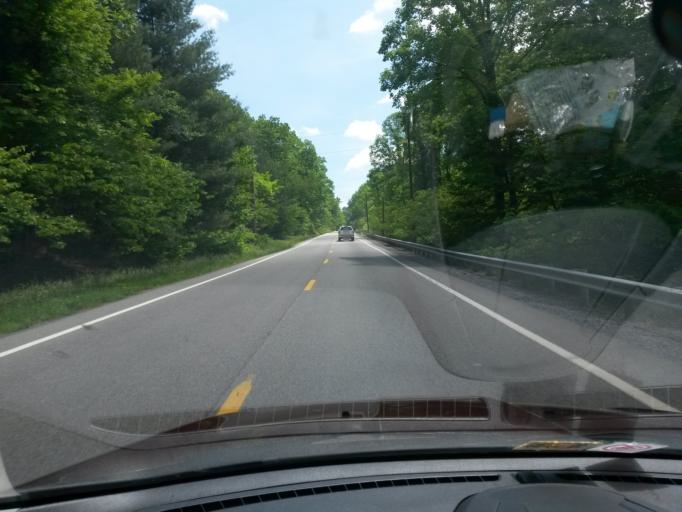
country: US
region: West Virginia
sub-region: Wyoming County
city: Pineville
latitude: 37.5528
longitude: -81.5596
